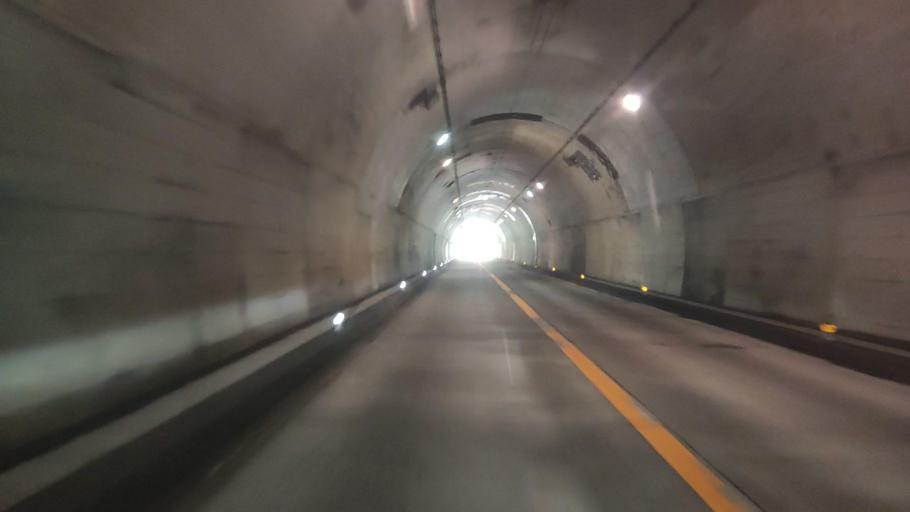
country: JP
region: Wakayama
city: Shingu
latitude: 33.8166
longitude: 135.8563
